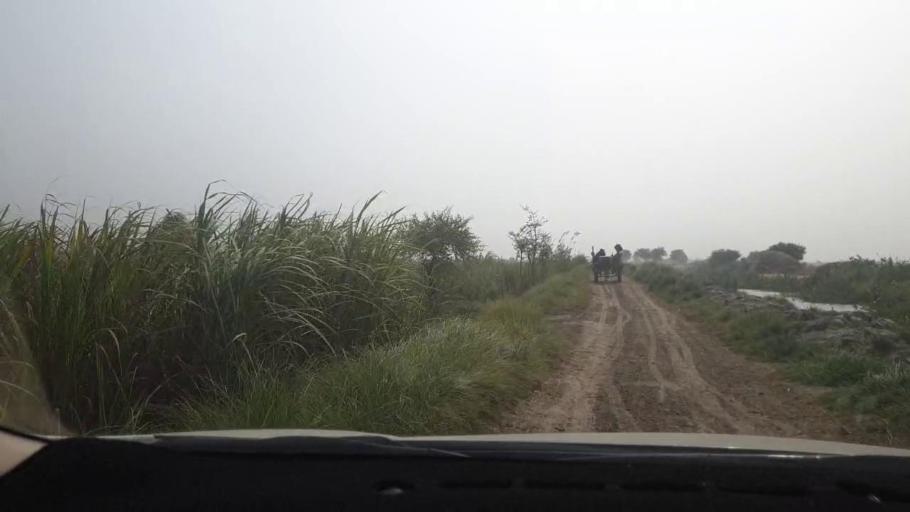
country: PK
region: Sindh
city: Tando Muhammad Khan
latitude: 25.0550
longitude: 68.5087
